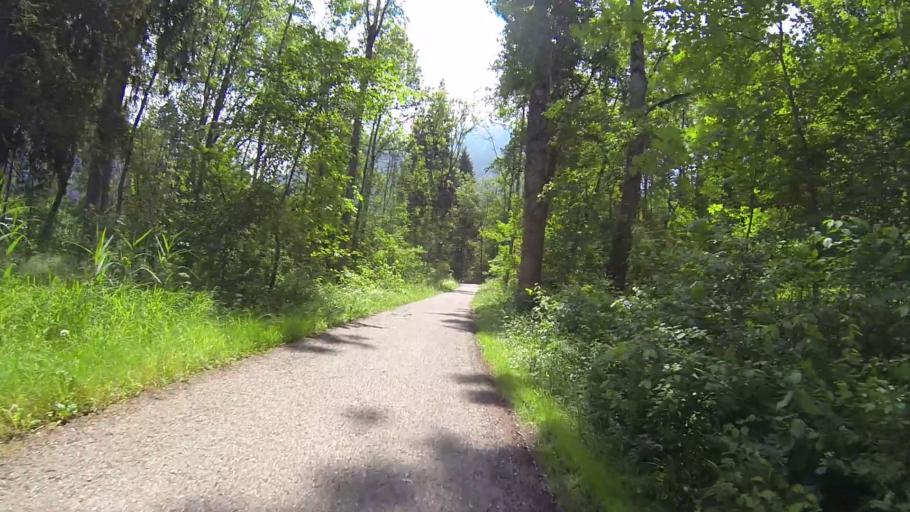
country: DE
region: Bavaria
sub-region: Swabia
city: Schwangau
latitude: 47.5601
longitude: 10.7311
